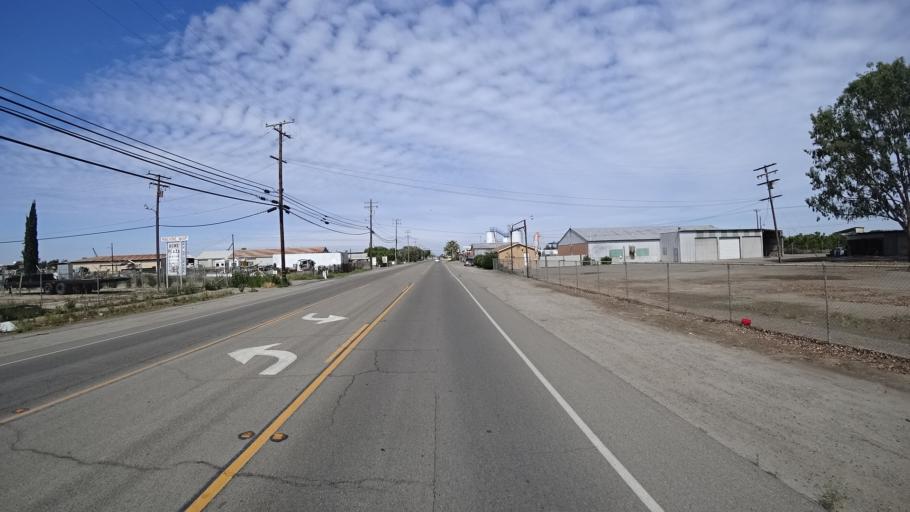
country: US
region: California
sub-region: Kings County
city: Hanford
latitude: 36.3280
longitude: -119.6208
